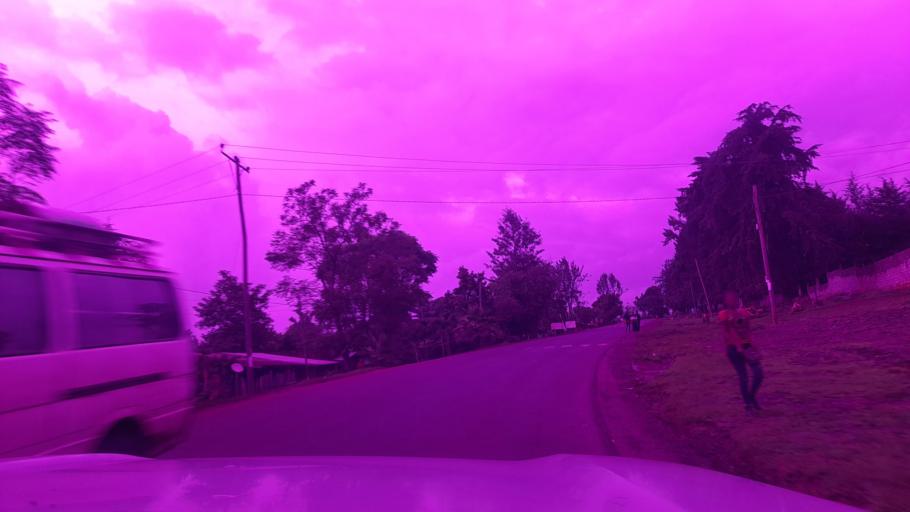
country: ET
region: Oromiya
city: Jima
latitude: 7.9621
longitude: 37.4407
